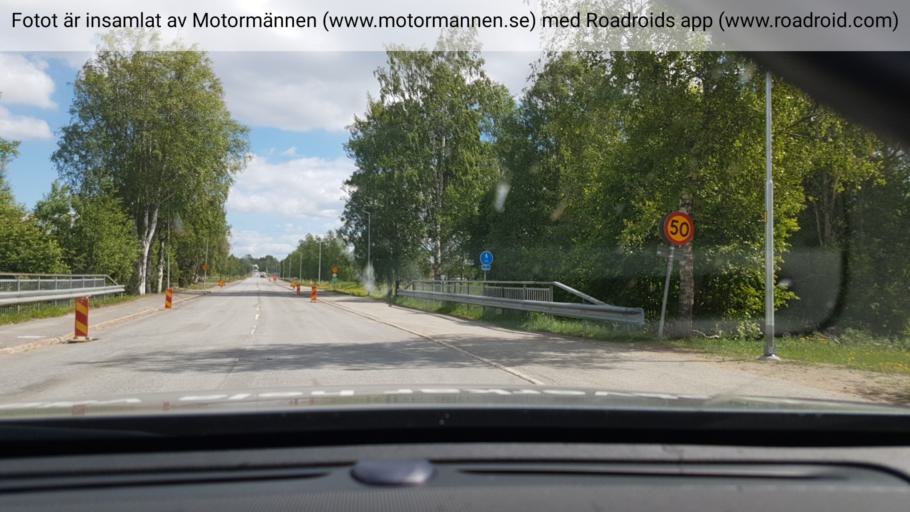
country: SE
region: Vaesterbotten
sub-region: Nordmalings Kommun
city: Nordmaling
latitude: 63.5688
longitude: 19.5061
